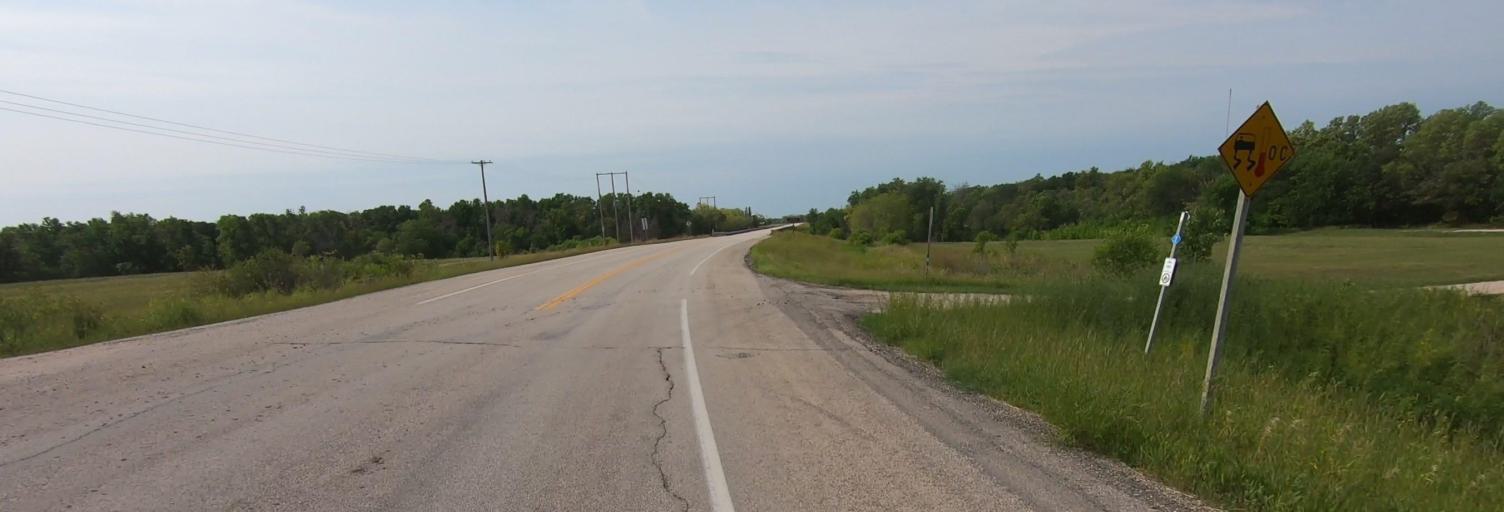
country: CA
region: Manitoba
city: Niverville
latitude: 49.5876
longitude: -97.1350
